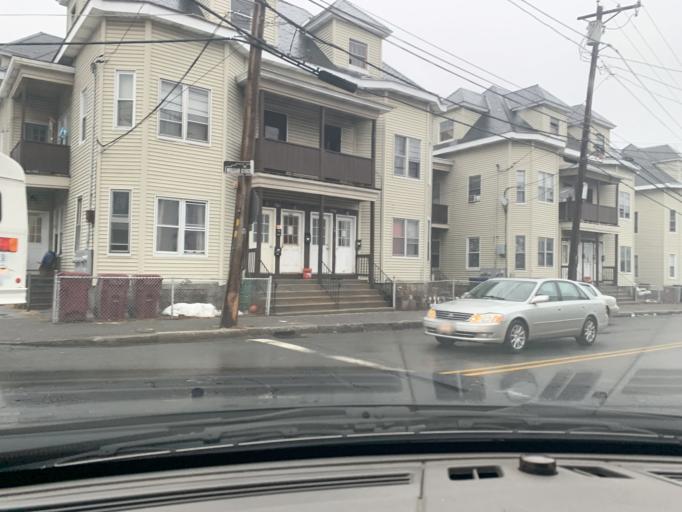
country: US
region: Massachusetts
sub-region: Middlesex County
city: Lowell
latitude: 42.6423
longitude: -71.3312
